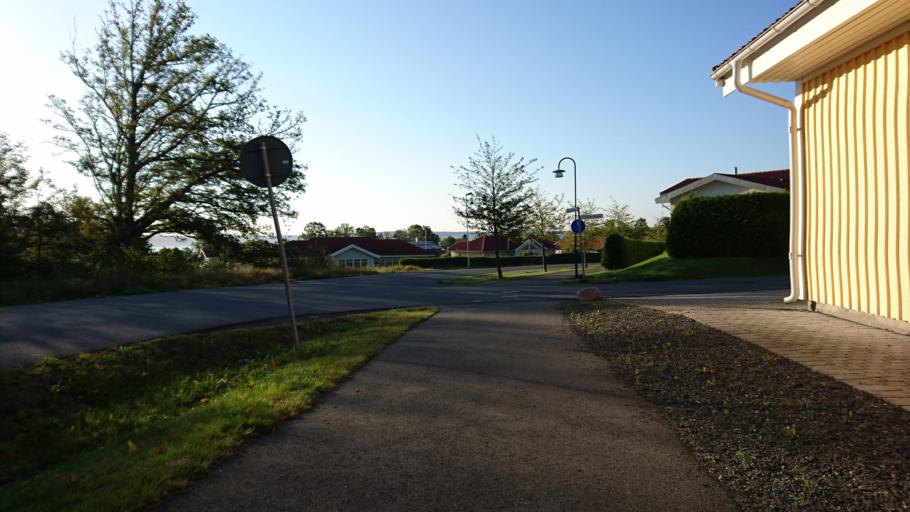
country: SE
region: Joenkoeping
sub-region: Jonkopings Kommun
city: Bankeryd
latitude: 57.8455
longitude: 14.1412
